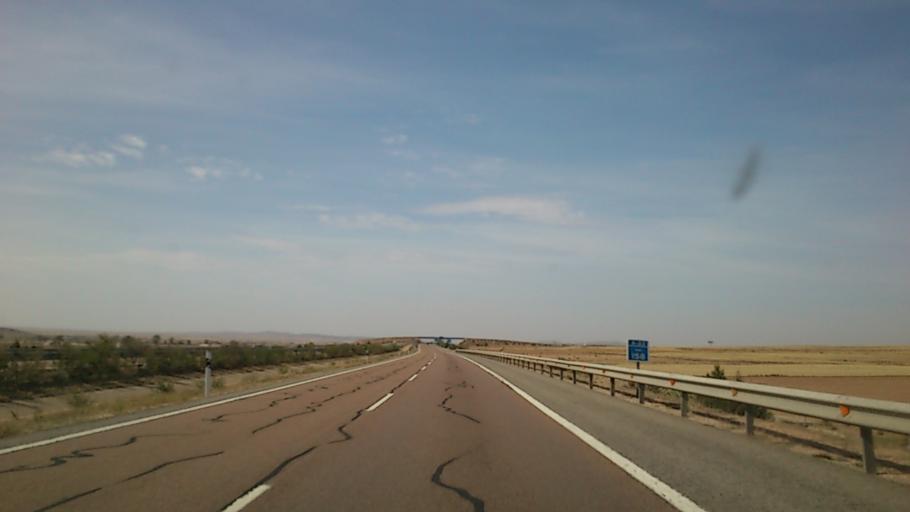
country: ES
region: Aragon
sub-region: Provincia de Teruel
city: Singra
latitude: 40.6815
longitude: -1.3155
